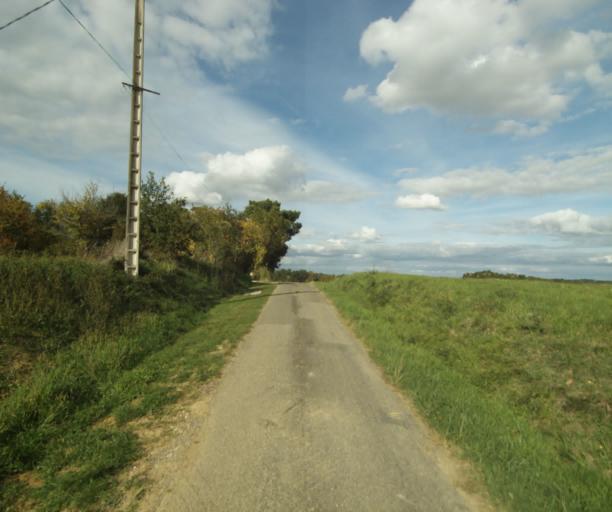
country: FR
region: Midi-Pyrenees
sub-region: Departement du Gers
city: Gondrin
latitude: 43.8475
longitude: 0.2750
